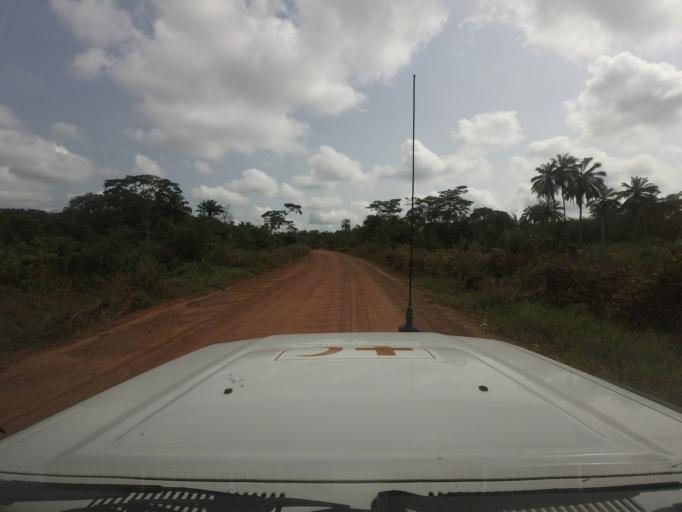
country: LR
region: Bong
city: Gbarnga
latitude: 7.2445
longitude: -9.4368
